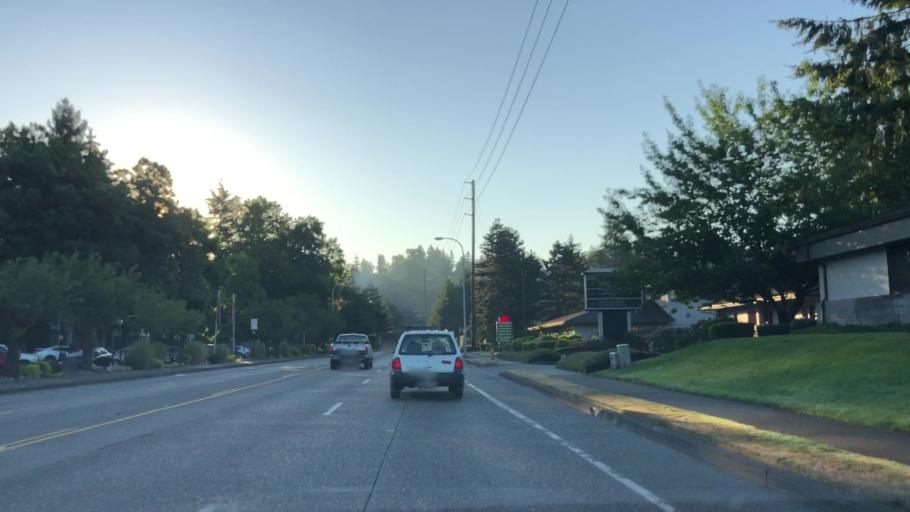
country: US
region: Washington
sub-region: King County
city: Auburn
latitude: 47.3152
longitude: -122.2121
